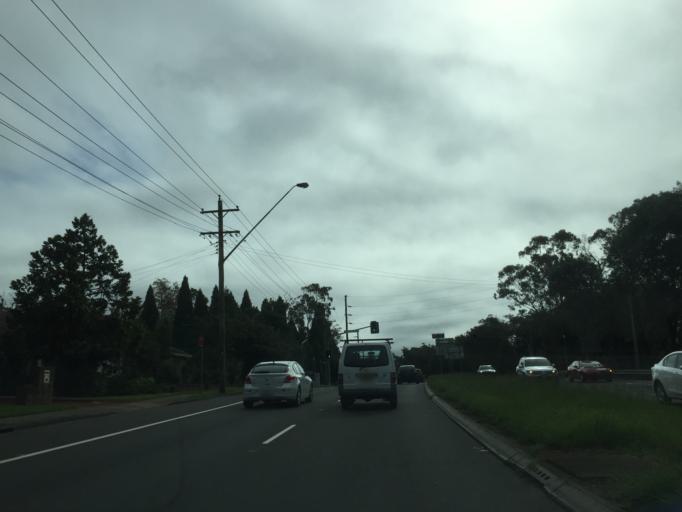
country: AU
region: New South Wales
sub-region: Blue Mountains Municipality
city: Blaxland
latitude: -33.7371
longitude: 150.6049
